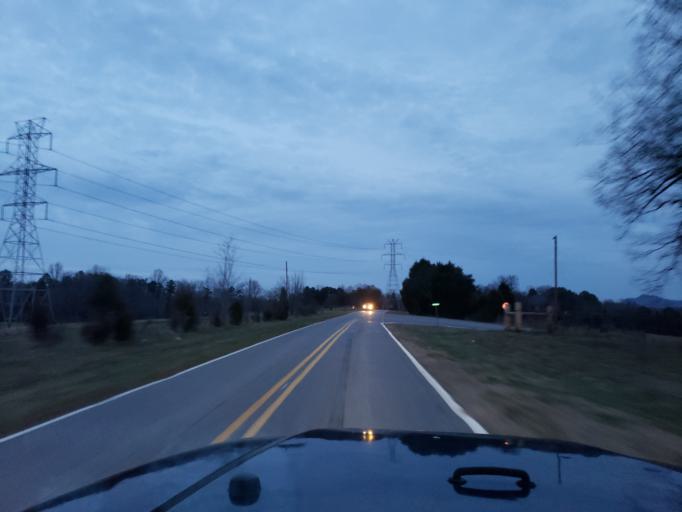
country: US
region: North Carolina
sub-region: Cleveland County
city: White Plains
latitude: 35.1782
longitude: -81.3916
